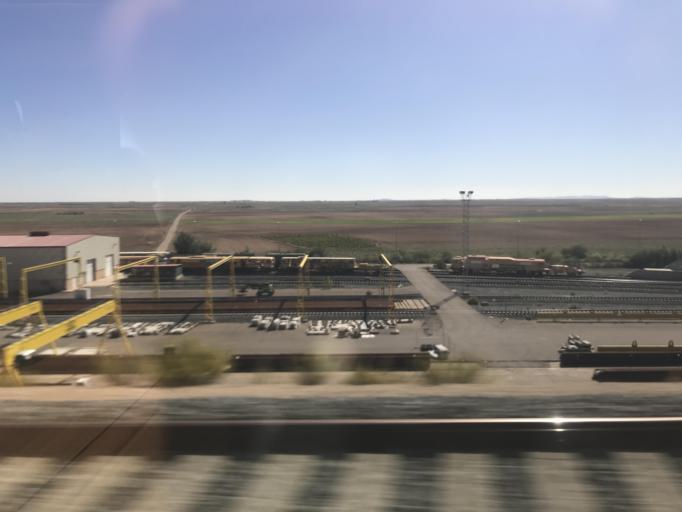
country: ES
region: Castille-La Mancha
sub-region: Province of Toledo
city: Villarrubia de Santiago
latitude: 39.9601
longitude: -3.3479
